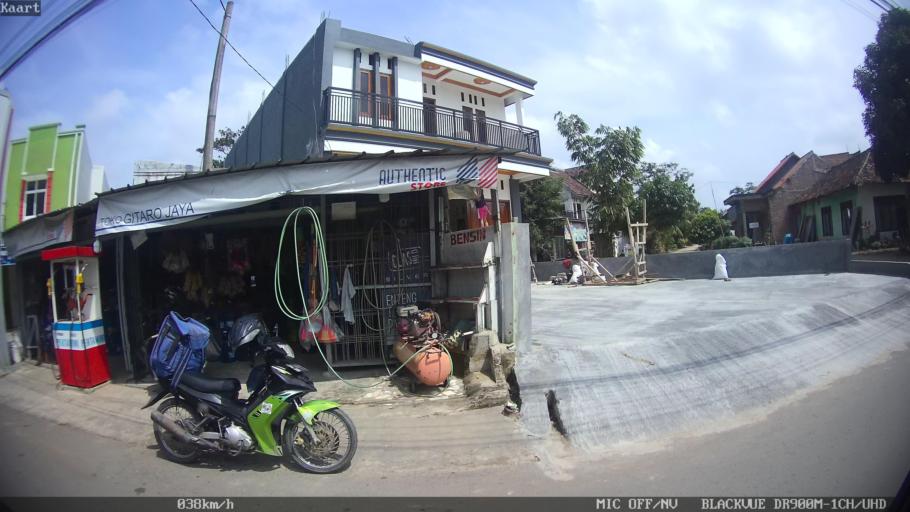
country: ID
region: Lampung
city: Kedaton
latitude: -5.3472
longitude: 105.2948
